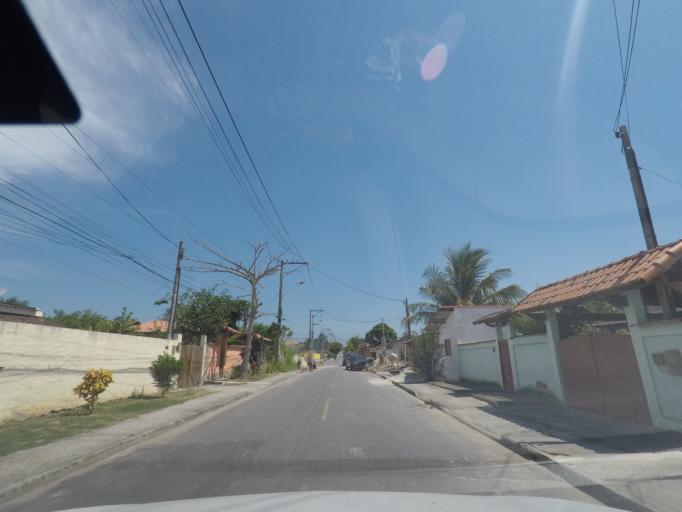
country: BR
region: Rio de Janeiro
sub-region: Marica
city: Marica
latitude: -22.9614
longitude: -42.9594
